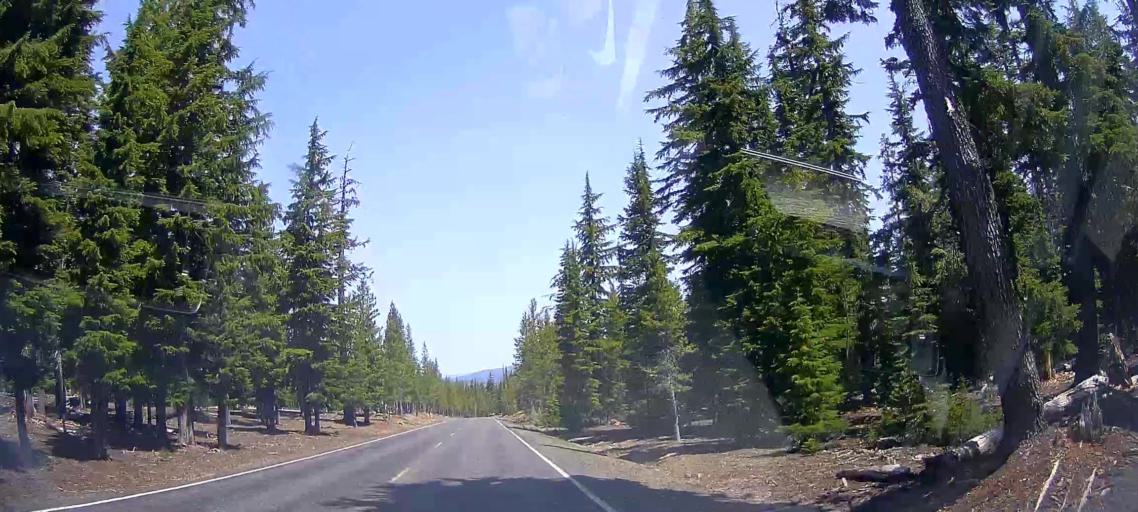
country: US
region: Oregon
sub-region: Jackson County
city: Shady Cove
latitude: 43.0019
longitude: -122.1344
